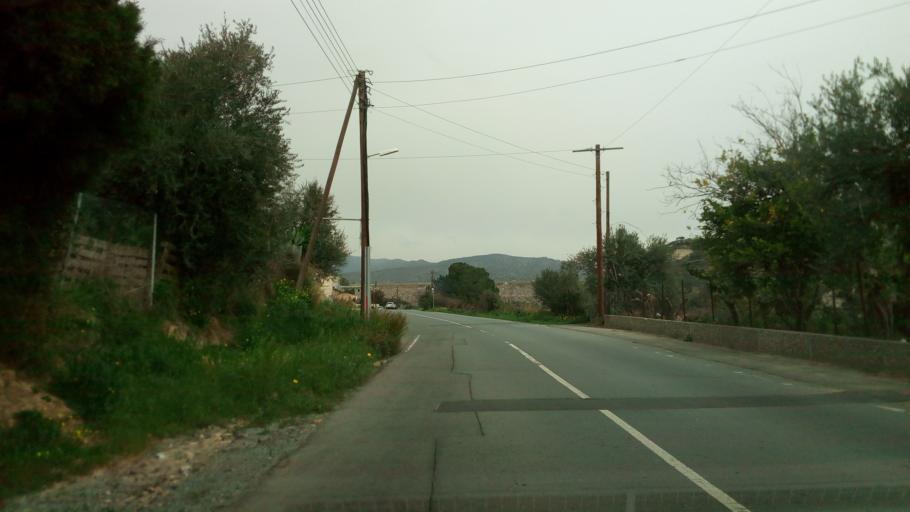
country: CY
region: Limassol
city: Mouttagiaka
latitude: 34.7381
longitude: 33.0835
